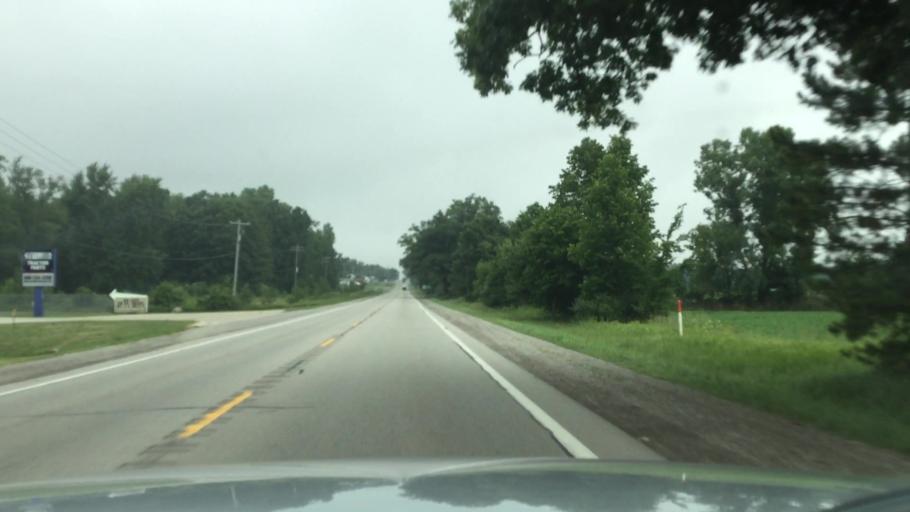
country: US
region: Michigan
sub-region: Shiawassee County
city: Durand
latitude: 42.9753
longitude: -83.9287
